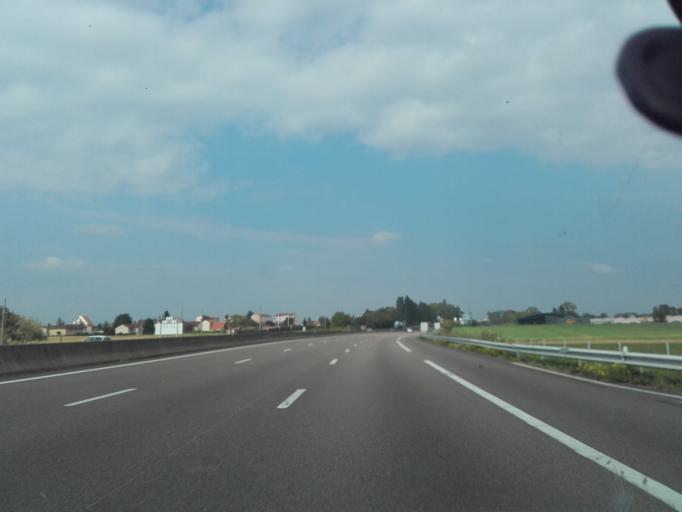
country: FR
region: Bourgogne
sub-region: Departement de Saone-et-Loire
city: Chatenoy-le-Royal
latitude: 46.7871
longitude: 4.8201
